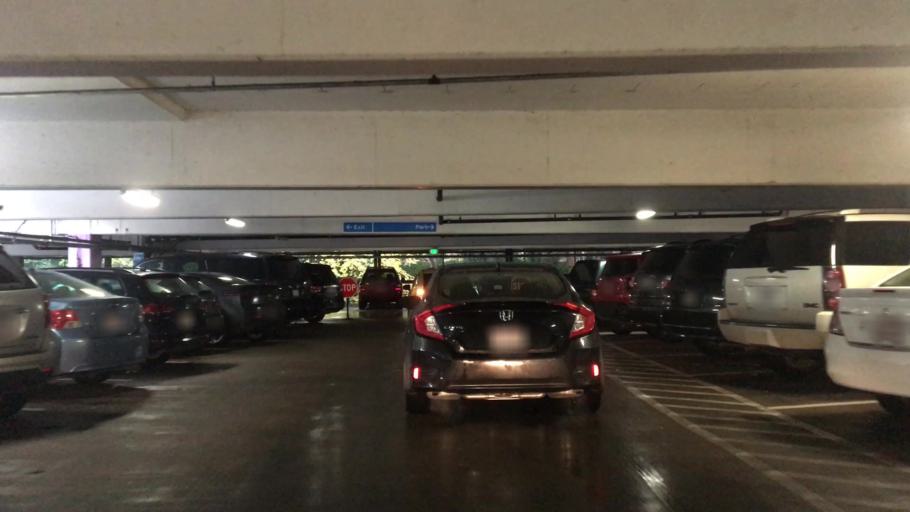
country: US
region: Washington
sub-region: King County
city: Yarrow Point
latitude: 47.6621
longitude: -122.2802
